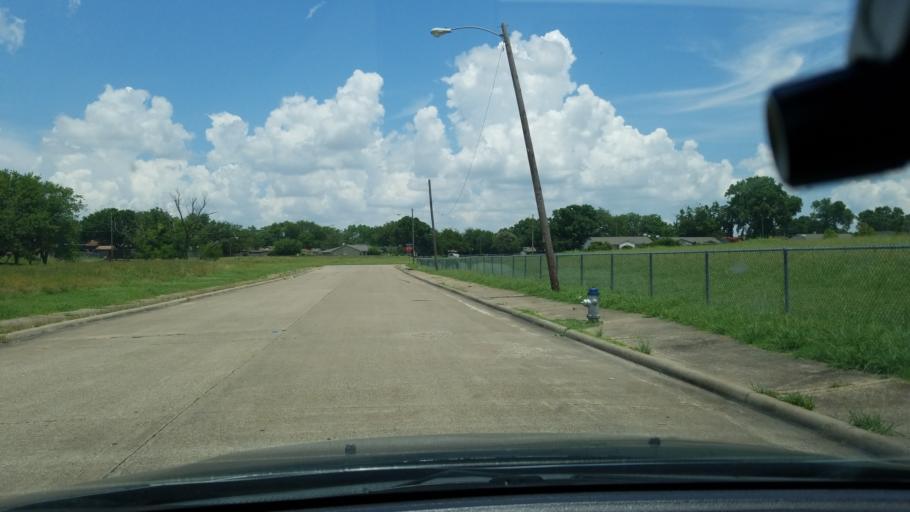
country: US
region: Texas
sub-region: Dallas County
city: Balch Springs
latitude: 32.7413
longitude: -96.6520
